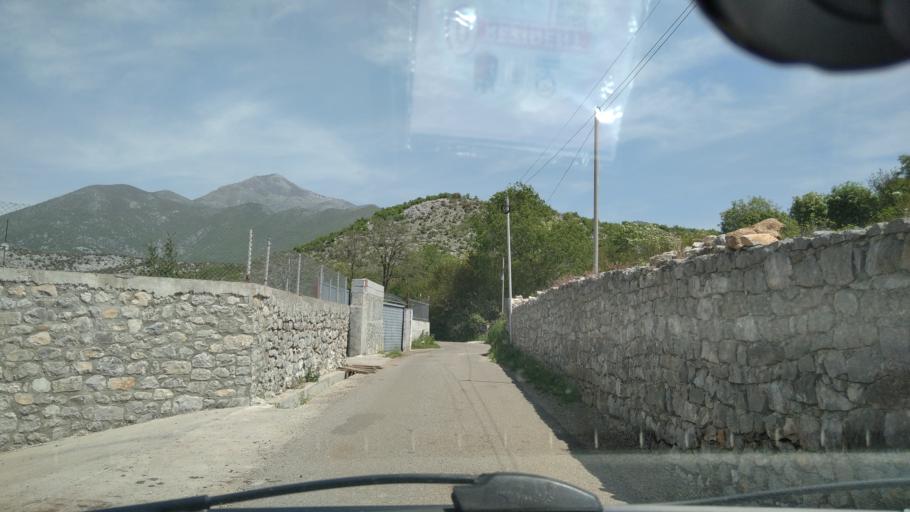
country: AL
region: Shkoder
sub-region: Rrethi i Malesia e Madhe
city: Gruemire
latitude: 42.1391
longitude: 19.5462
